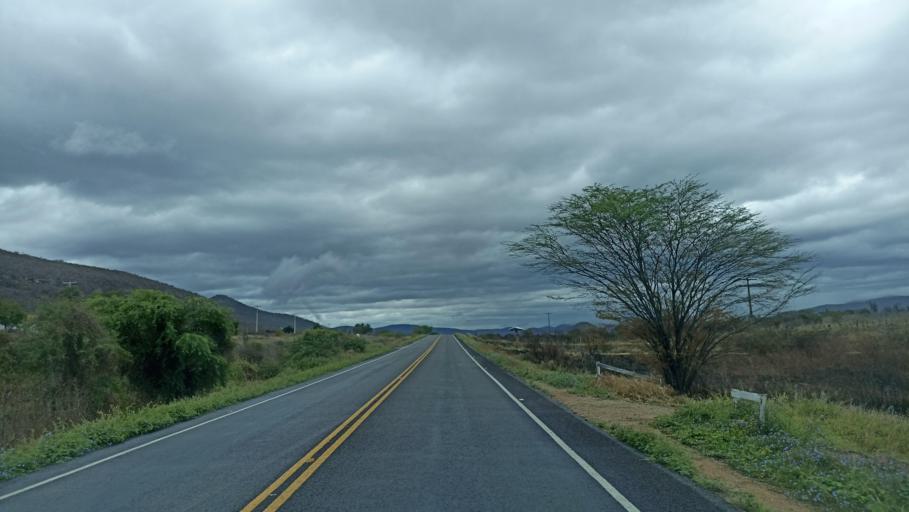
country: BR
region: Bahia
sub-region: Iacu
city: Iacu
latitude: -12.8797
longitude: -40.3897
